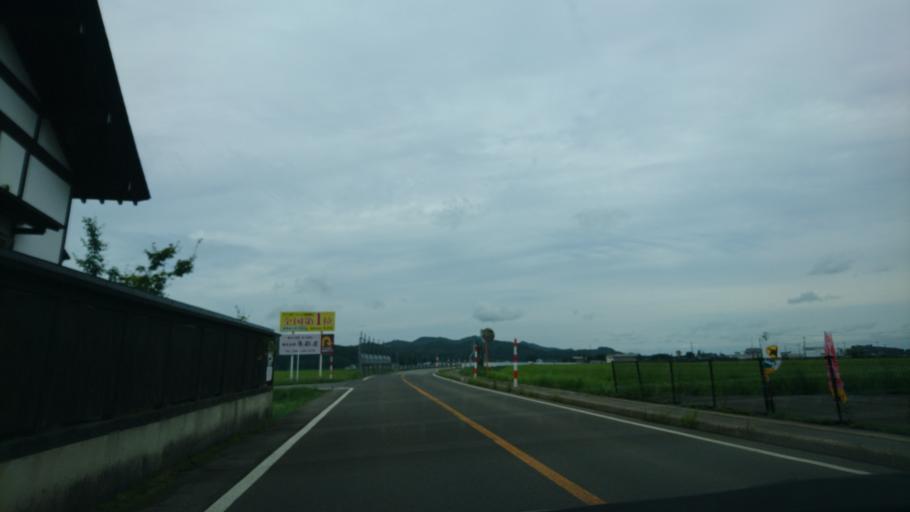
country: JP
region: Akita
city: Yuzawa
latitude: 39.1559
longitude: 140.5663
